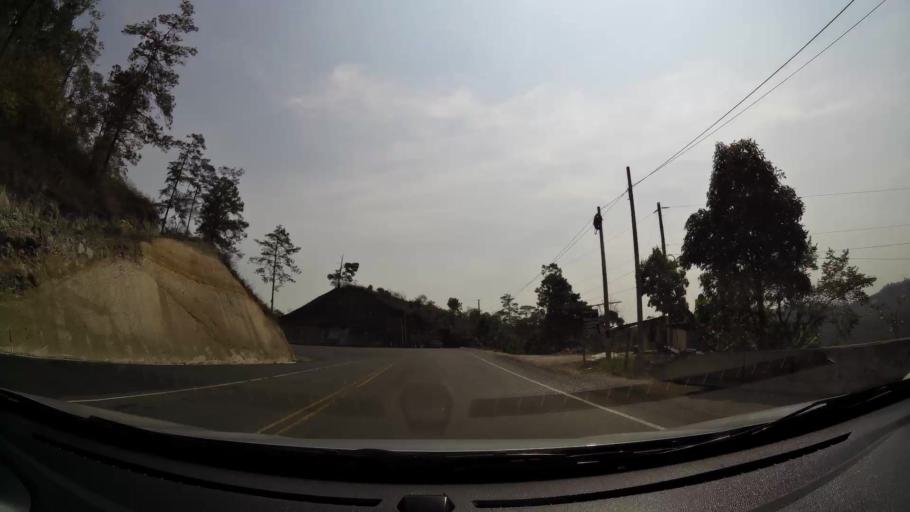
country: HN
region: Comayagua
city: Potrerillos
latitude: 14.5534
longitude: -87.8211
